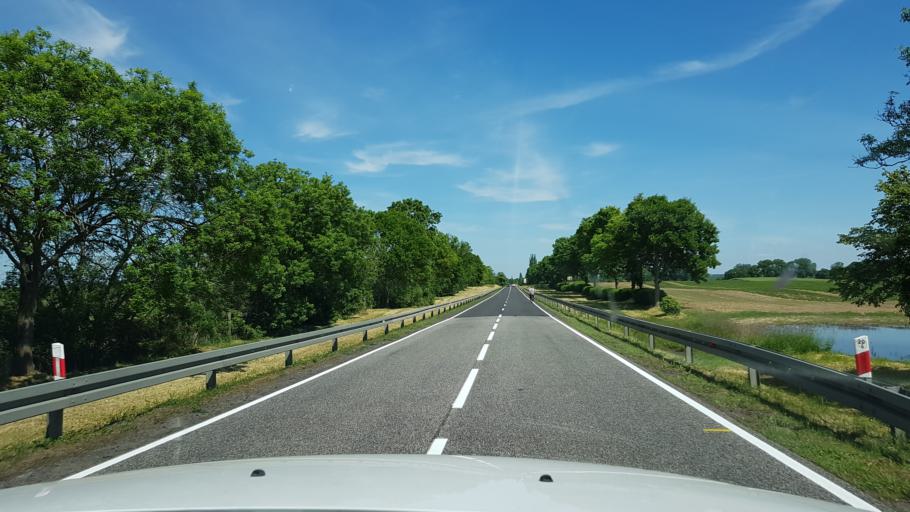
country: PL
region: West Pomeranian Voivodeship
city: Trzcinsko Zdroj
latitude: 52.9585
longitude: 14.5388
